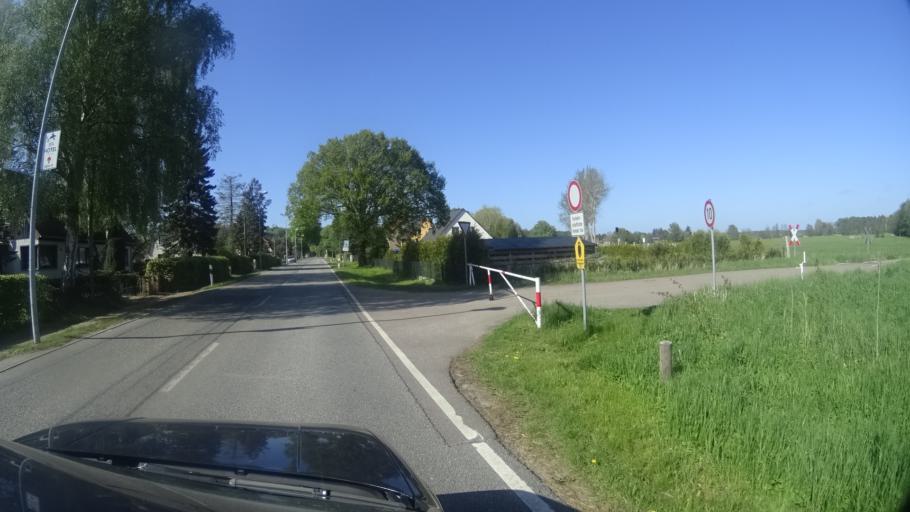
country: DE
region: Mecklenburg-Vorpommern
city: Seeheilbad Graal-Muritz
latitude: 54.2398
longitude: 12.2250
